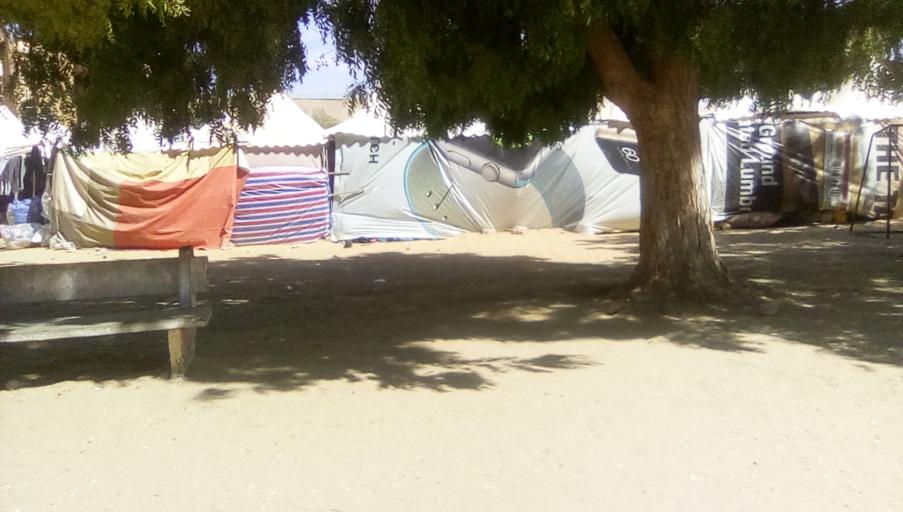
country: SN
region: Saint-Louis
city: Saint-Louis
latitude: 16.0657
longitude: -16.4214
